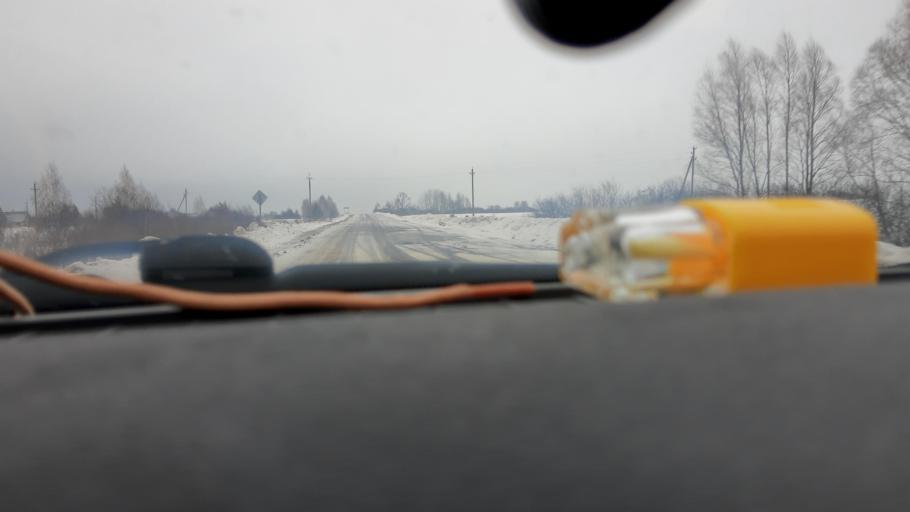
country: RU
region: Bashkortostan
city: Iglino
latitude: 54.6338
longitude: 56.4250
